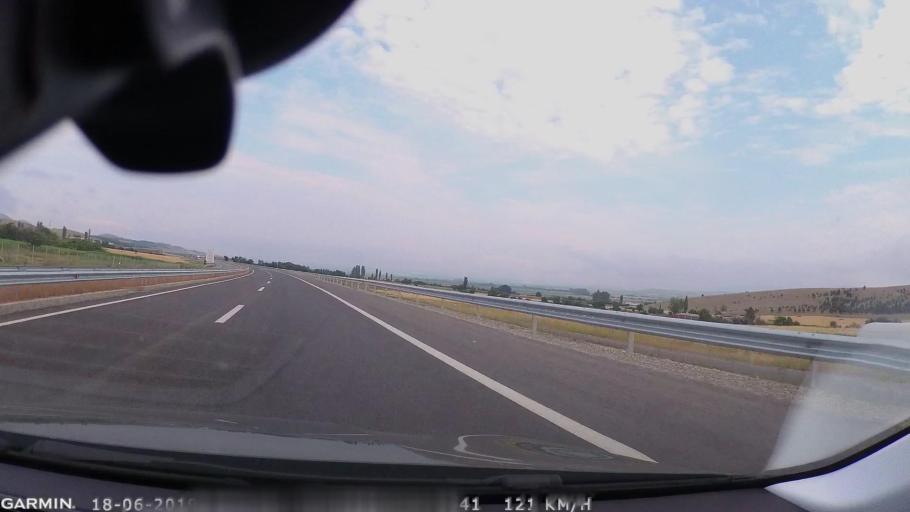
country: MK
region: Stip
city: Shtip
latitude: 41.7879
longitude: 22.1153
